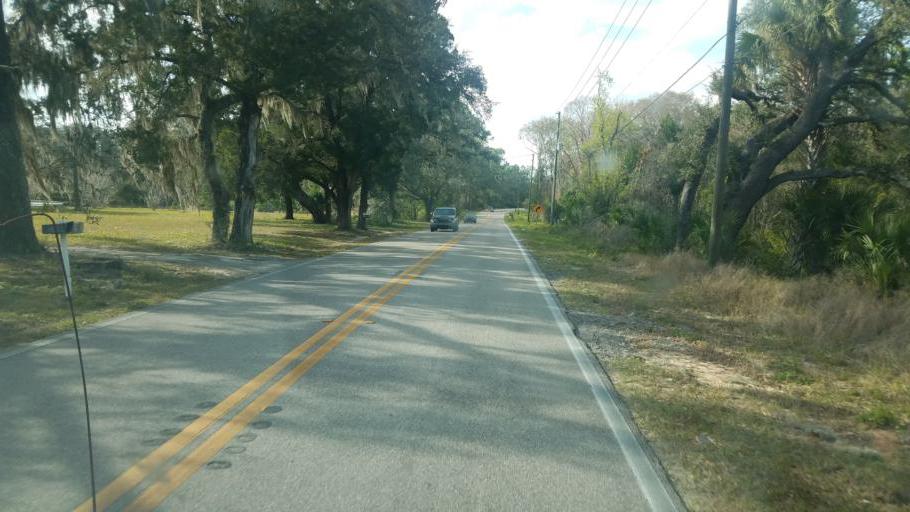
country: US
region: Florida
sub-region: Polk County
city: Loughman
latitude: 28.2546
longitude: -81.5756
